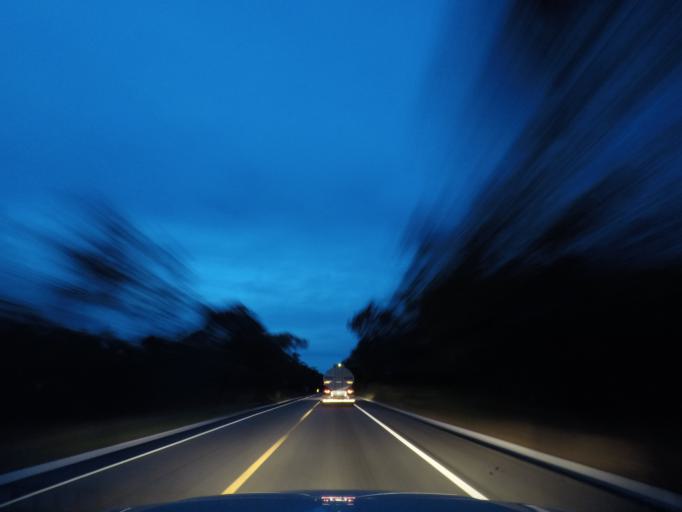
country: BR
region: Bahia
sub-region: Andarai
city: Vera Cruz
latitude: -12.4920
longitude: -41.3378
